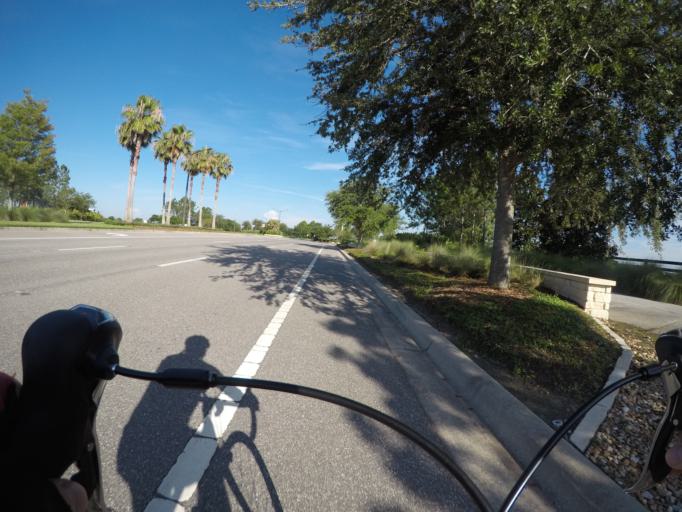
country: US
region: Florida
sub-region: Osceola County
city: Buenaventura Lakes
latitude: 28.3695
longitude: -81.2855
